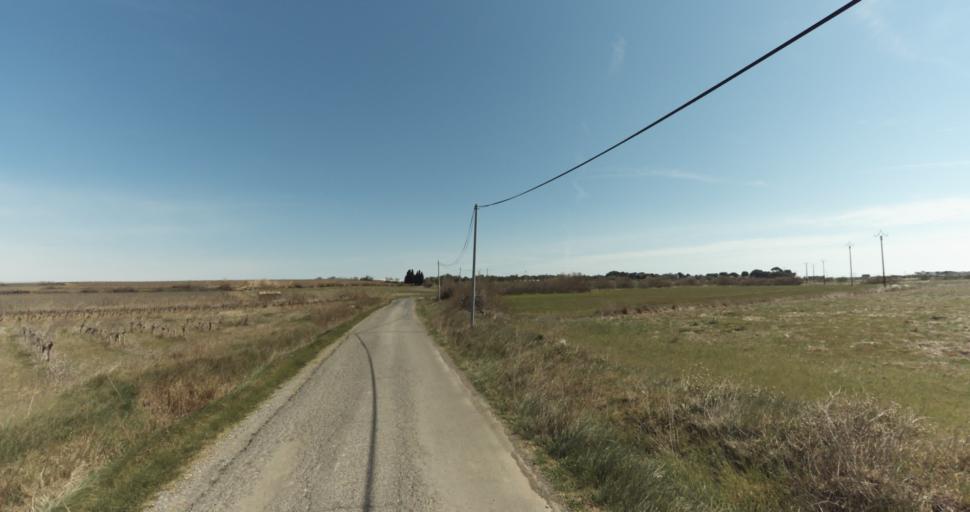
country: FR
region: Languedoc-Roussillon
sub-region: Departement de l'Herault
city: Marseillan
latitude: 43.3869
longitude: 3.5471
